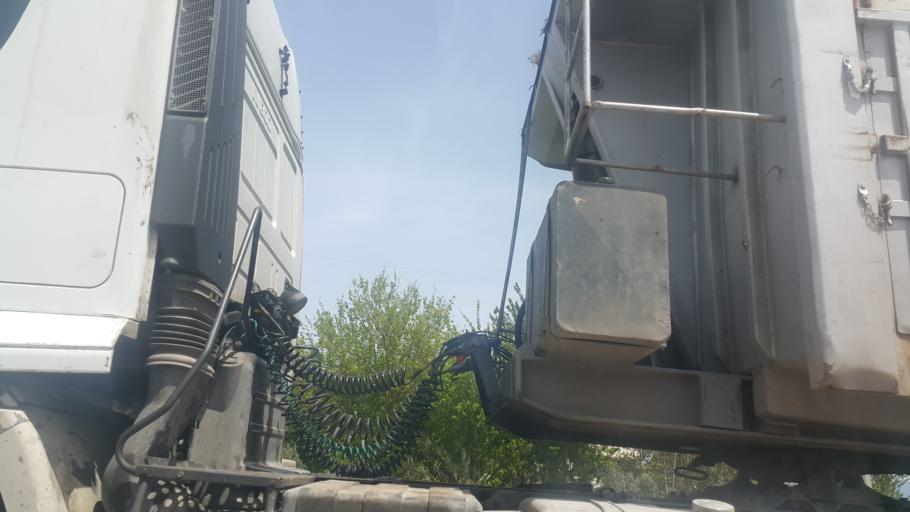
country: TR
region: Osmaniye
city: Toprakkale
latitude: 37.0569
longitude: 36.1219
